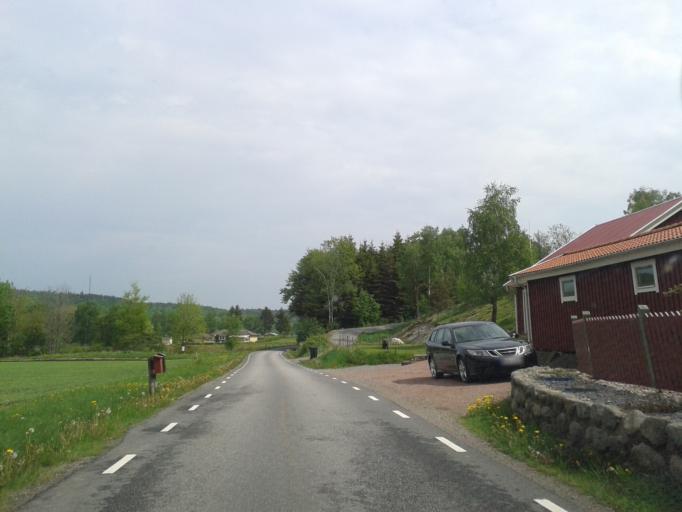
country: SE
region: Vaestra Goetaland
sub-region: Kungalvs Kommun
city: Kungalv
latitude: 57.9215
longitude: 11.9599
